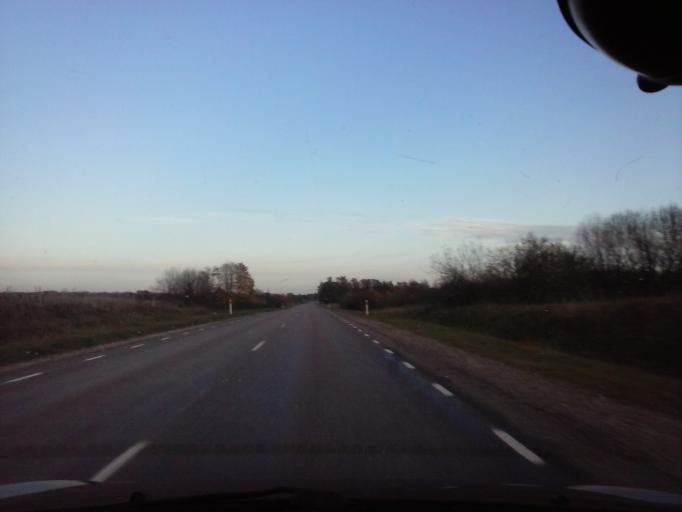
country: EE
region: Harju
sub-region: Nissi vald
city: Turba
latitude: 58.9172
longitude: 24.1746
